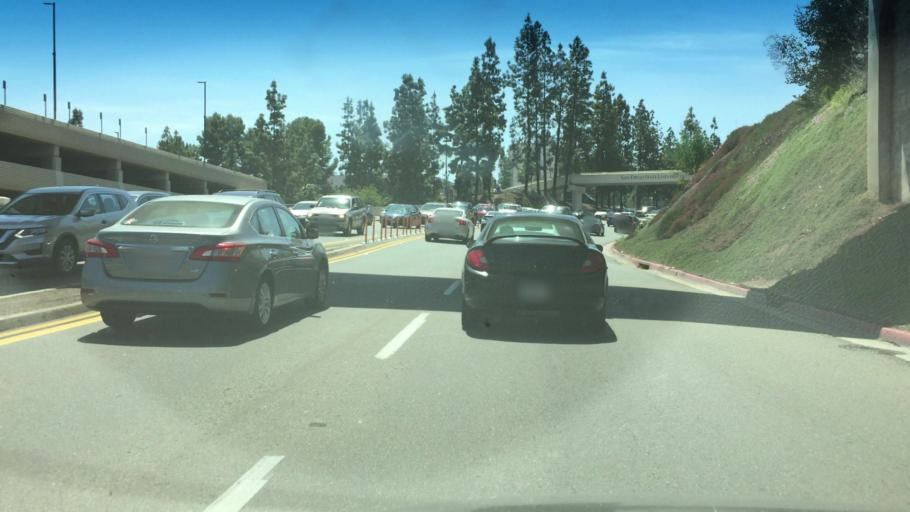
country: US
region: California
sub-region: San Diego County
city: La Mesa
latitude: 32.7756
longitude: -117.0680
